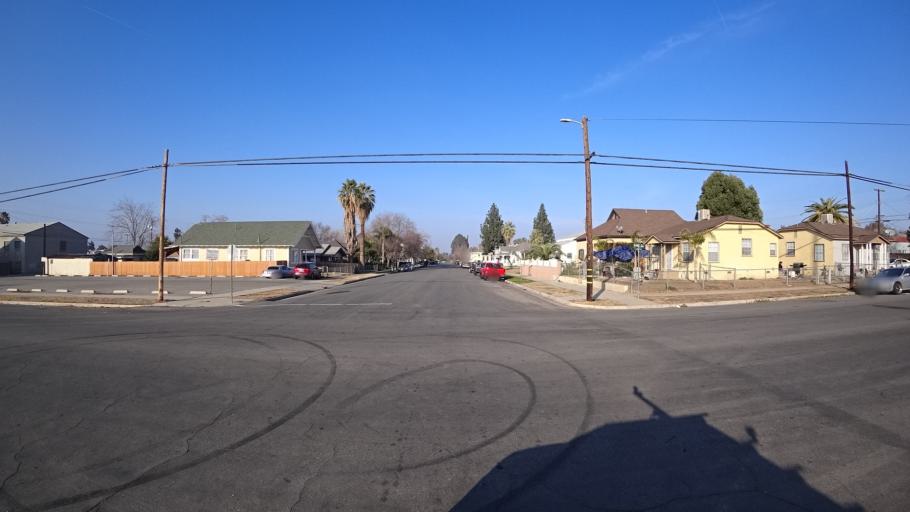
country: US
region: California
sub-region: Kern County
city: Bakersfield
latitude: 35.3827
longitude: -118.9890
